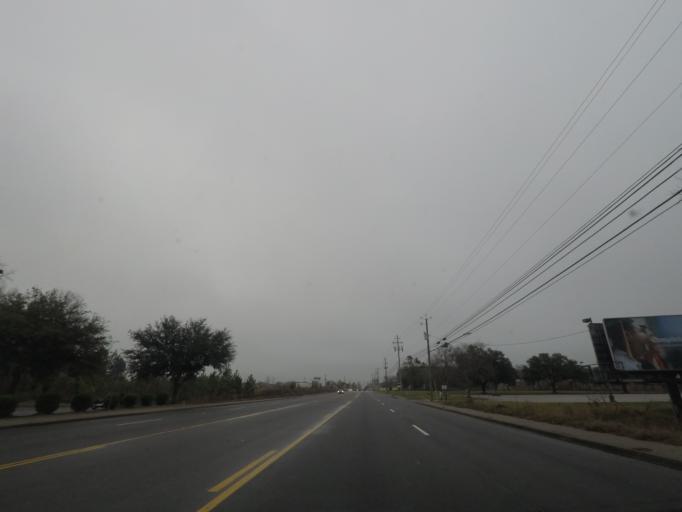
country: US
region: South Carolina
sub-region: Clarendon County
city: Manning
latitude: 33.6985
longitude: -80.2308
